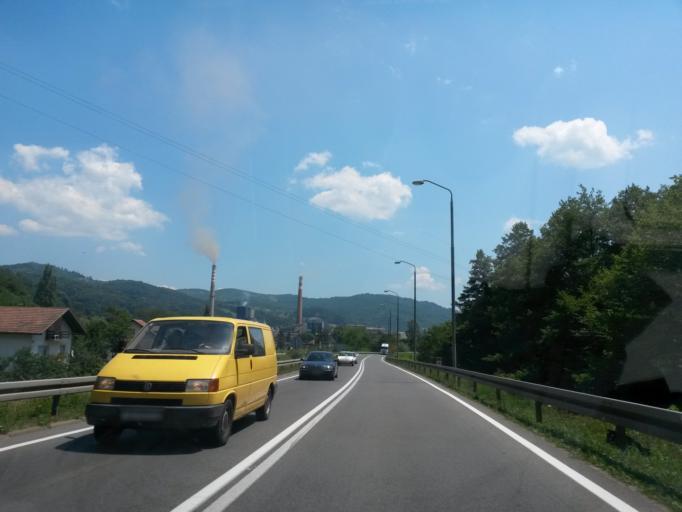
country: BA
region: Federation of Bosnia and Herzegovina
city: Maglaj
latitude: 44.5302
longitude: 18.0889
